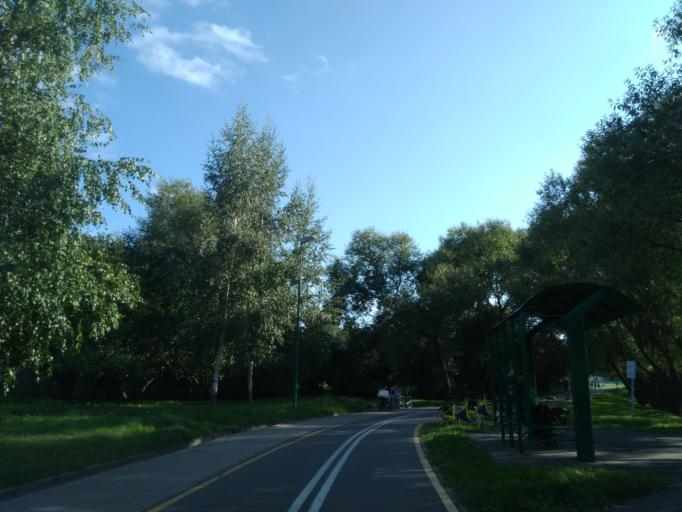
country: BY
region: Minsk
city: Minsk
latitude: 53.8806
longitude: 27.5755
